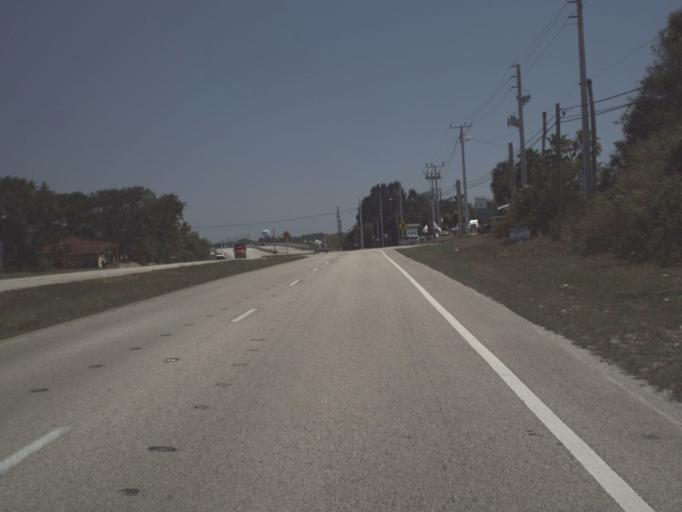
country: US
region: Florida
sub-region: Indian River County
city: Roseland
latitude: 27.8589
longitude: -80.4922
